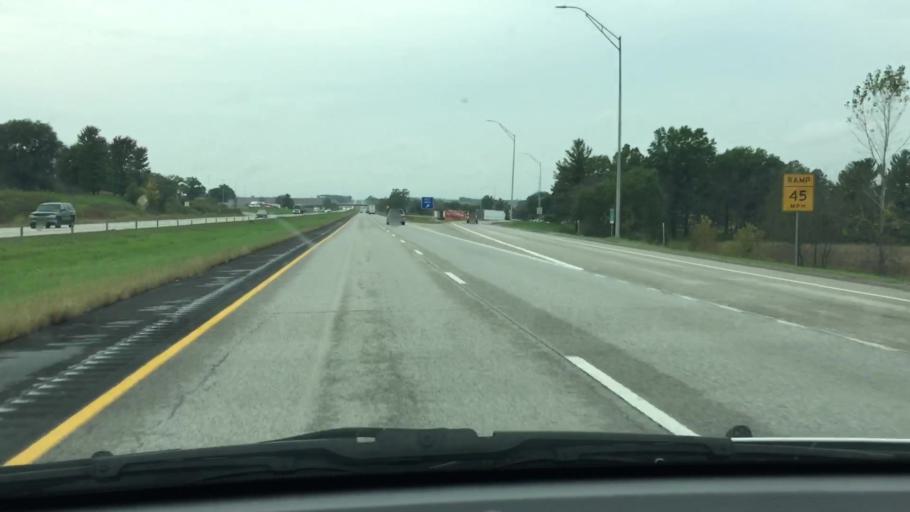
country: US
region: Iowa
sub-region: Johnson County
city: Tiffin
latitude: 41.6943
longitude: -91.6763
